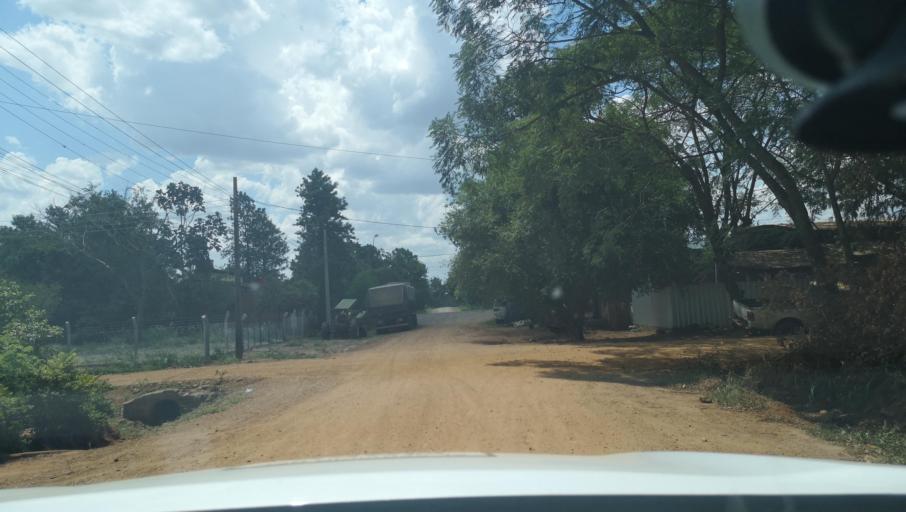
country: PY
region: Itapua
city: Carmen del Parana
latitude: -27.1567
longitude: -56.2486
